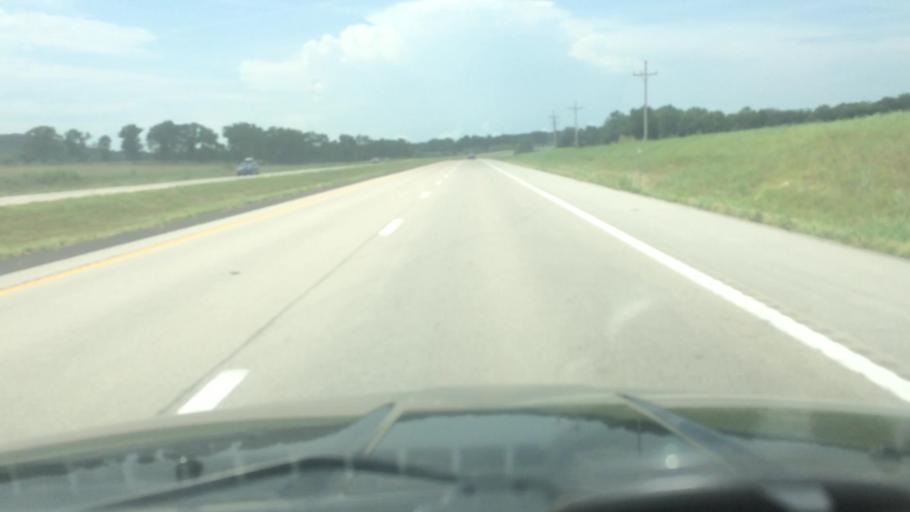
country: US
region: Missouri
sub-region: Polk County
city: Humansville
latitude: 37.8165
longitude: -93.6104
